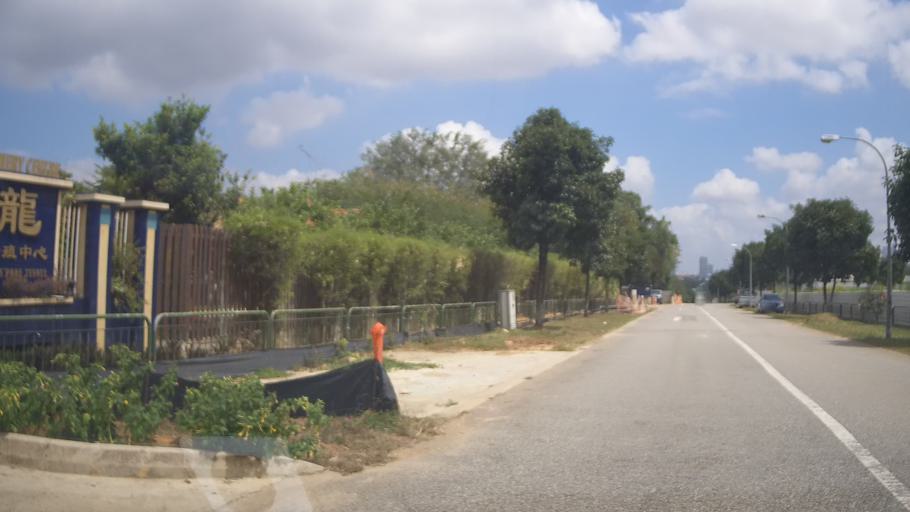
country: MY
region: Johor
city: Johor Bahru
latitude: 1.4371
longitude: 103.7256
